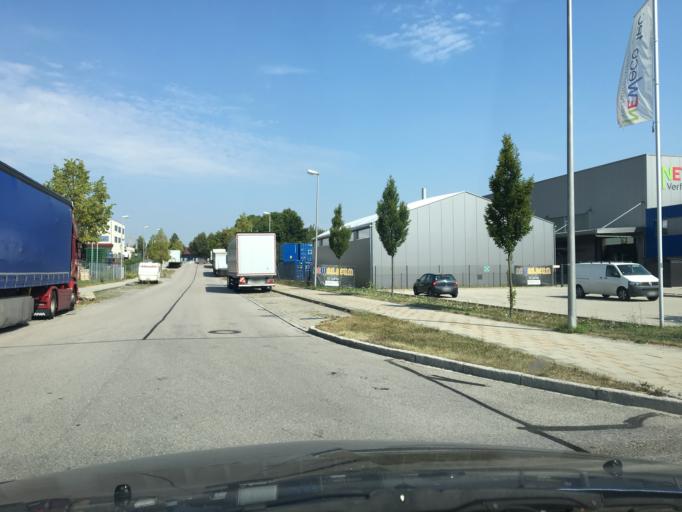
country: DE
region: Bavaria
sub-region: Upper Bavaria
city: Muehldorf
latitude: 48.2556
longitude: 12.5430
